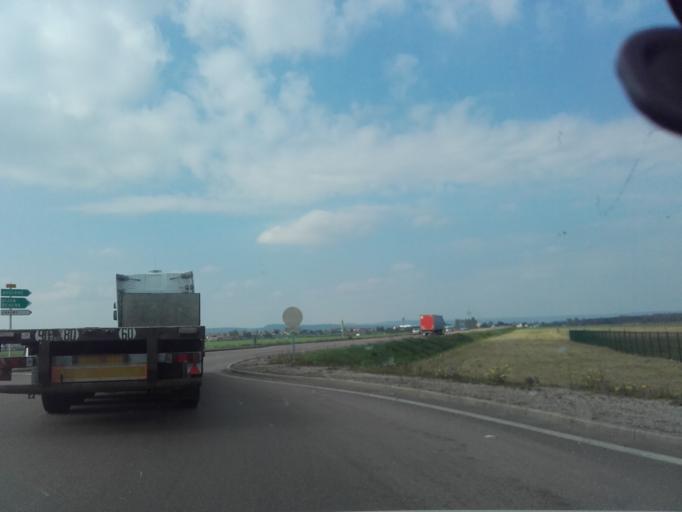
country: FR
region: Bourgogne
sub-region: Departement de Saone-et-Loire
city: Champforgeuil
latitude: 46.8304
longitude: 4.8255
